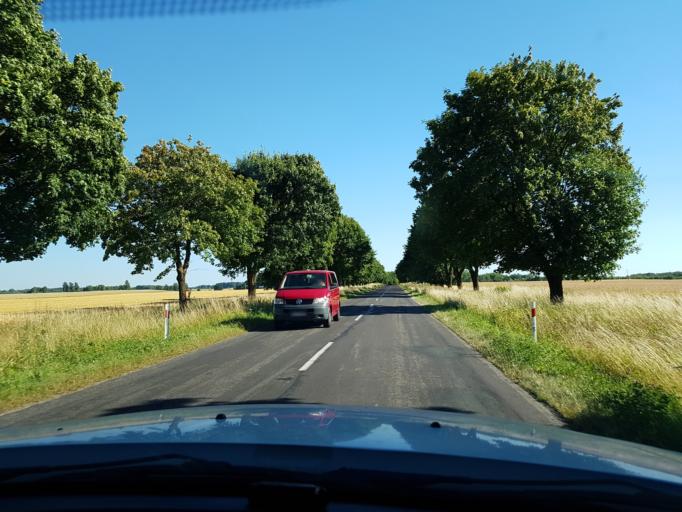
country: PL
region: West Pomeranian Voivodeship
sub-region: Powiat lobeski
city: Lobez
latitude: 53.6916
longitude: 15.6071
